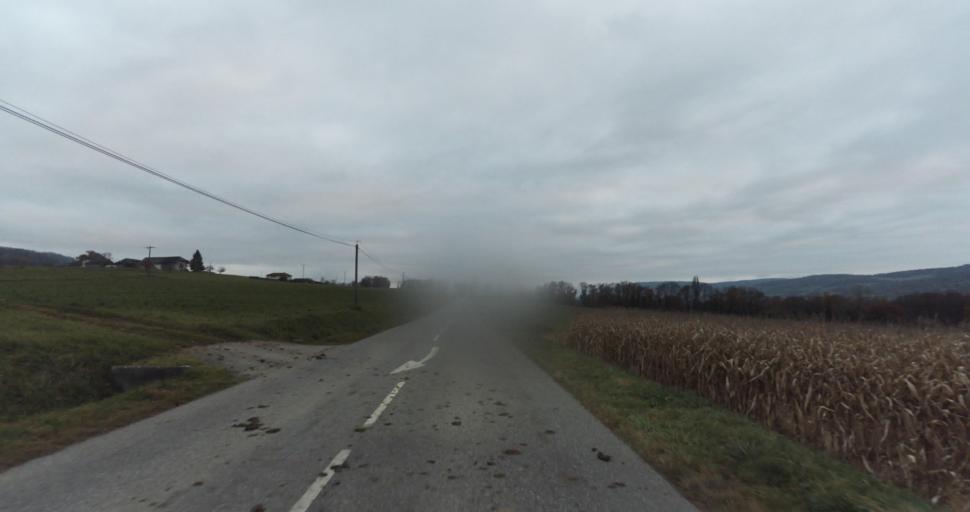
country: FR
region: Rhone-Alpes
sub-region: Departement de la Haute-Savoie
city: Saint-Felix
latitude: 45.8175
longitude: 5.9742
